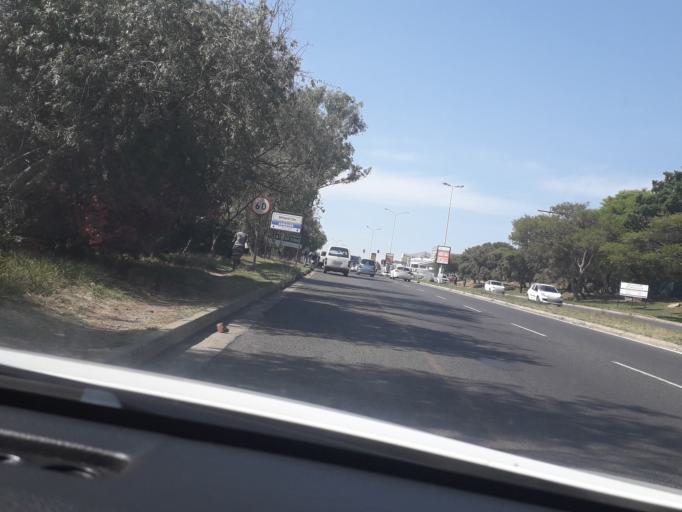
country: ZA
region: Gauteng
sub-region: City of Johannesburg Metropolitan Municipality
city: Diepsloot
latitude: -26.0618
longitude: 28.0211
